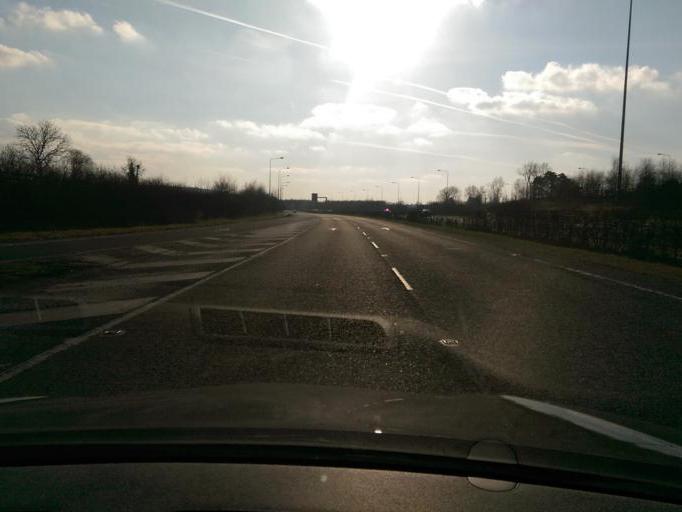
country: IE
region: Leinster
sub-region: Kildare
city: Monasterevin
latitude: 53.1447
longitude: -7.0198
